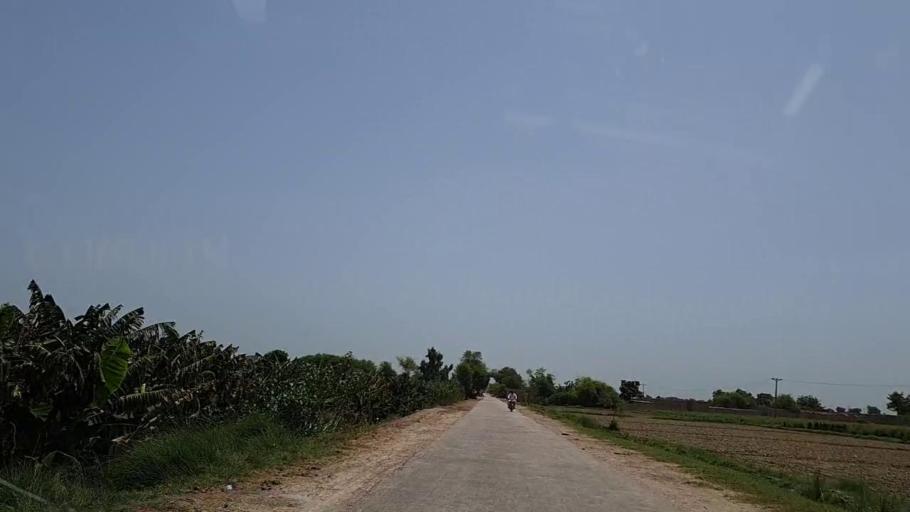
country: PK
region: Sindh
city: Tharu Shah
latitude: 26.9593
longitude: 68.0671
